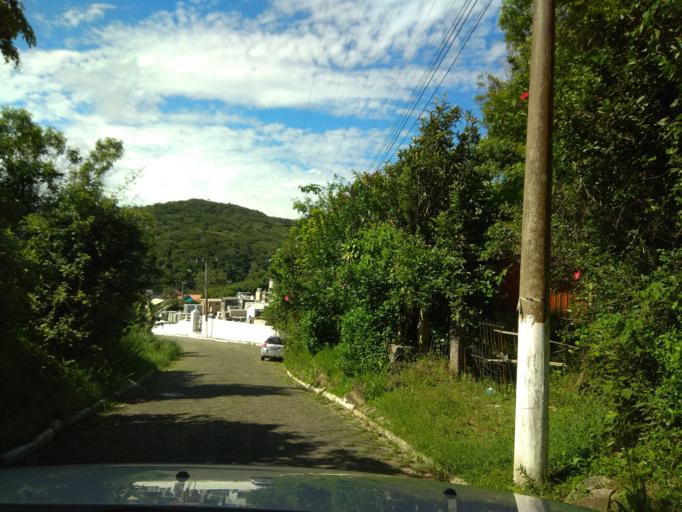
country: BR
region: Santa Catarina
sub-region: Laguna
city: Laguna
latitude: -28.4839
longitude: -48.7752
